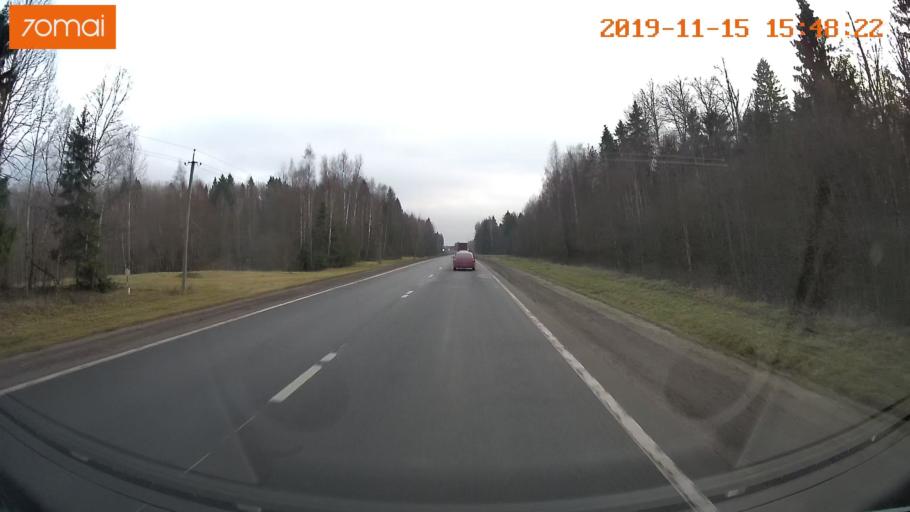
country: RU
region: Jaroslavl
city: Danilov
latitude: 57.9280
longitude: 40.0065
